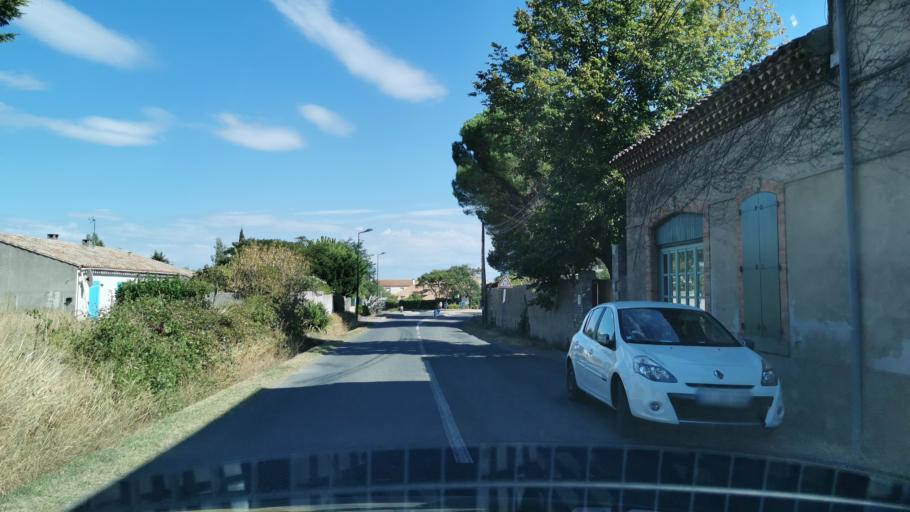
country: FR
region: Languedoc-Roussillon
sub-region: Departement de l'Aude
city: Peyriac-Minervois
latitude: 43.3134
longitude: 2.5558
